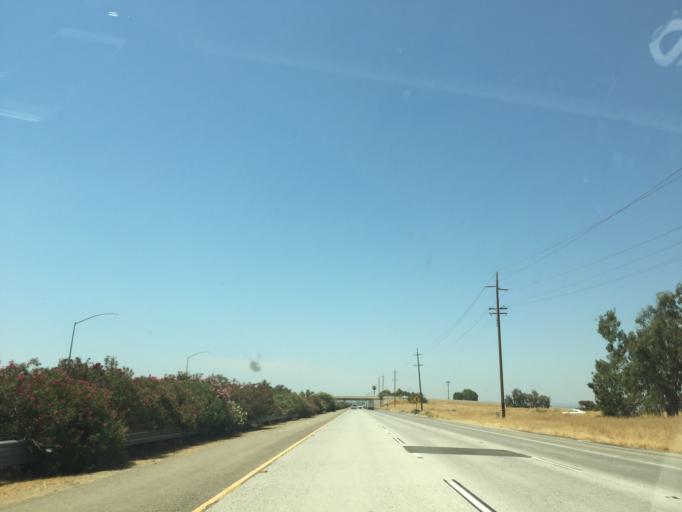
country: US
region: California
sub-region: Kern County
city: Weedpatch
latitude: 35.0533
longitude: -118.9664
